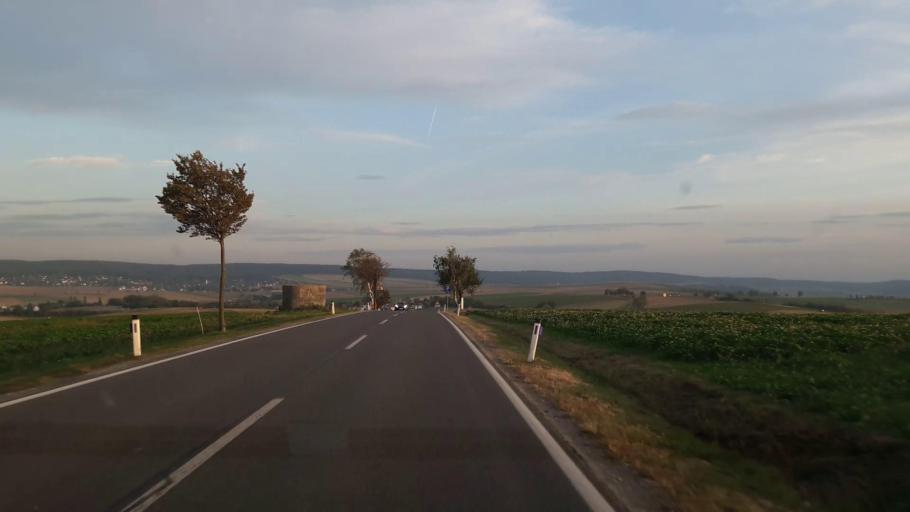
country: AT
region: Lower Austria
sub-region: Politischer Bezirk Korneuburg
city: Grossrussbach
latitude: 48.4488
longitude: 16.3836
